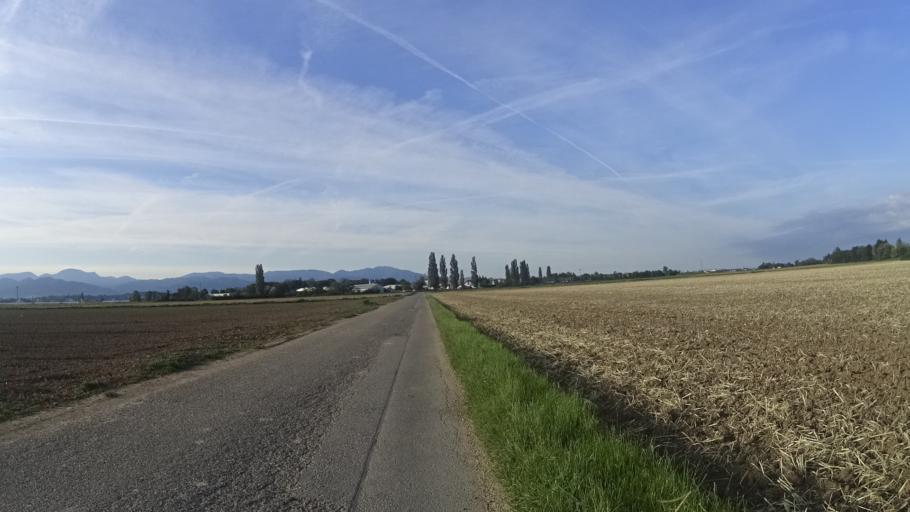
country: DE
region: Baden-Wuerttemberg
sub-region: Freiburg Region
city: Hartheim
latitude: 47.9455
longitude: 7.6477
